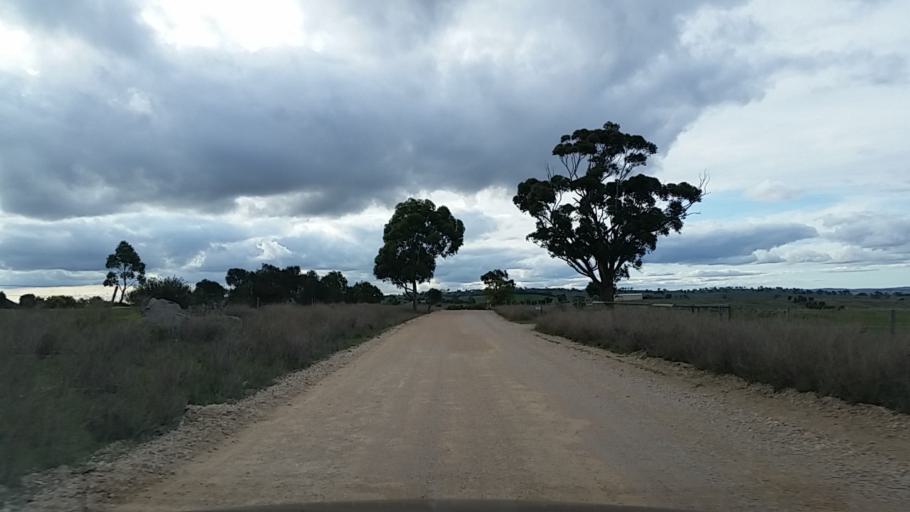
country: AU
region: South Australia
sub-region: Mount Barker
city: Callington
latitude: -34.9845
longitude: 139.0578
